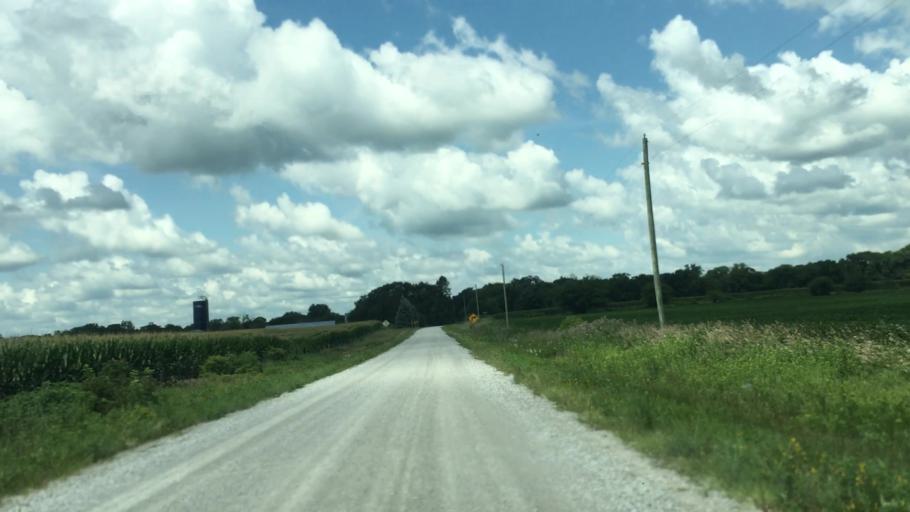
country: US
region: Iowa
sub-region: Linn County
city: Lisbon
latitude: 41.8281
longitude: -91.3876
